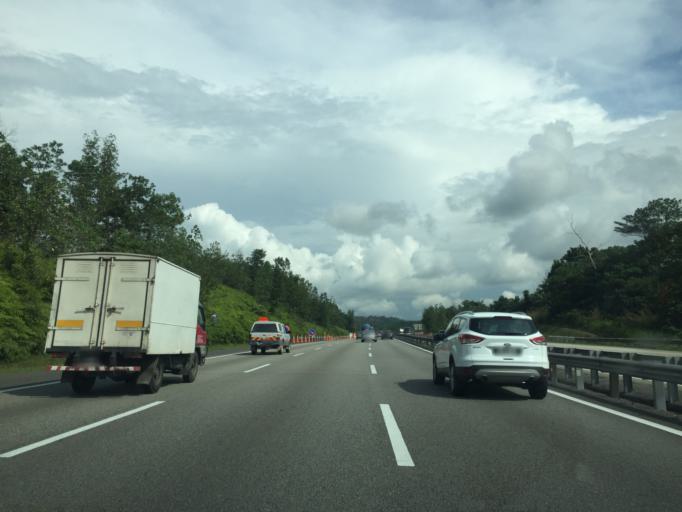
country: MY
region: Selangor
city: Batang Berjuntai
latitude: 3.5400
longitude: 101.5186
